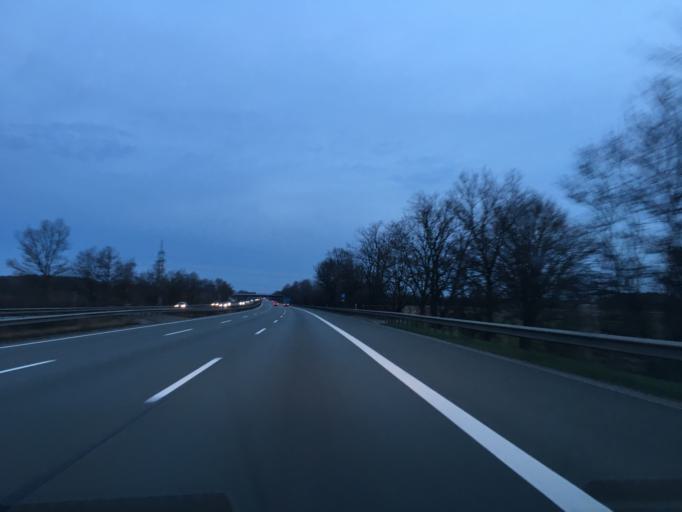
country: DE
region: Lower Saxony
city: Seevetal
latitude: 53.3986
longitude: 10.0262
